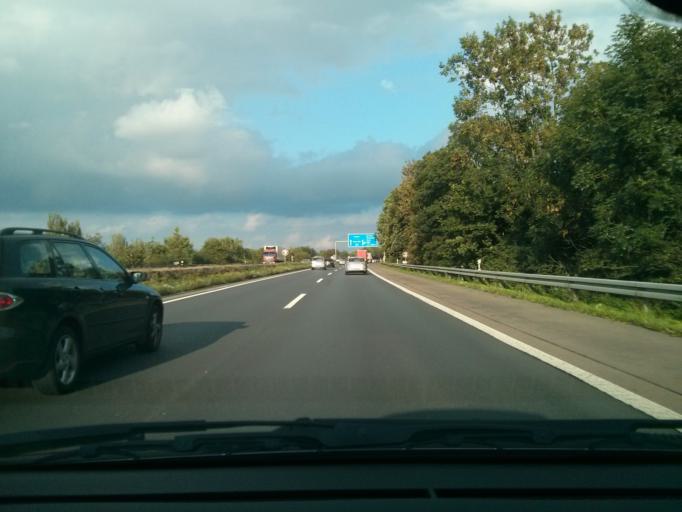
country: DE
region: North Rhine-Westphalia
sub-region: Regierungsbezirk Arnsberg
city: Holzwickede
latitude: 51.5192
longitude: 7.6377
